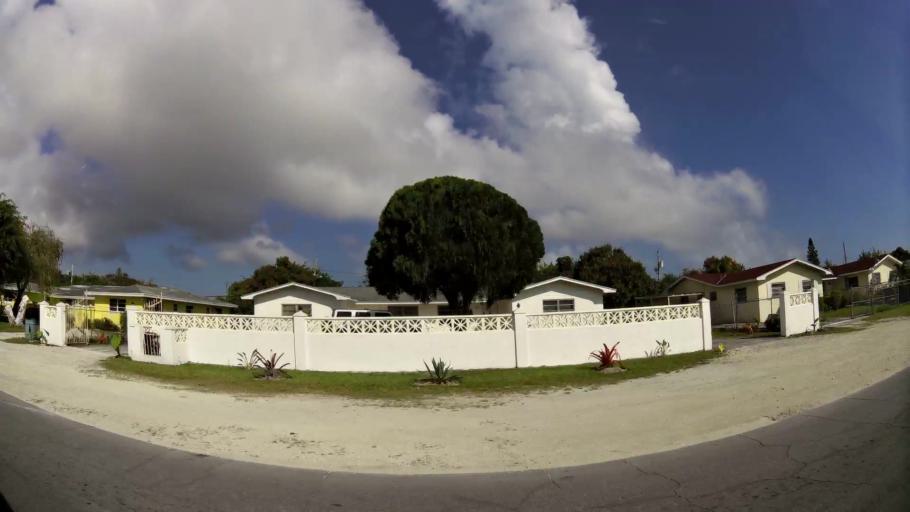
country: BS
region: Freeport
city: Freeport
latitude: 26.5203
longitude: -78.6871
